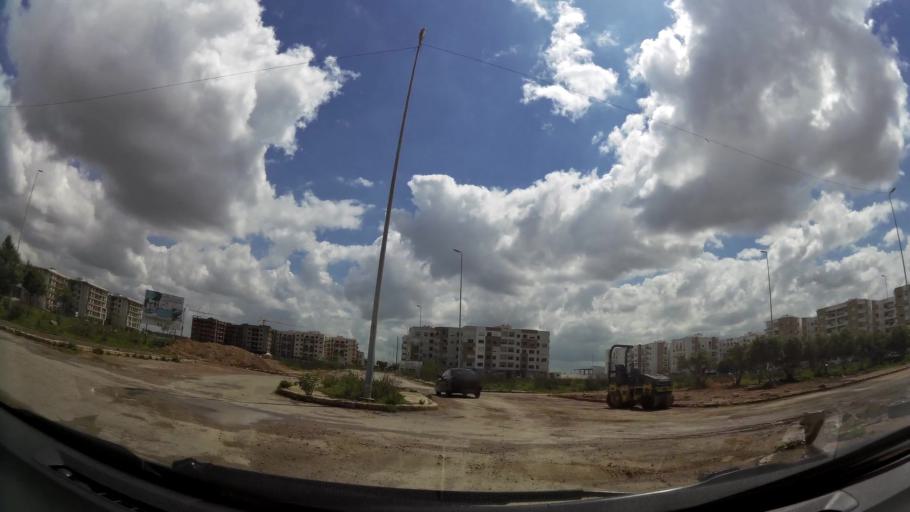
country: MA
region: Chaouia-Ouardigha
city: Nouaseur
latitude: 33.3939
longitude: -7.5624
